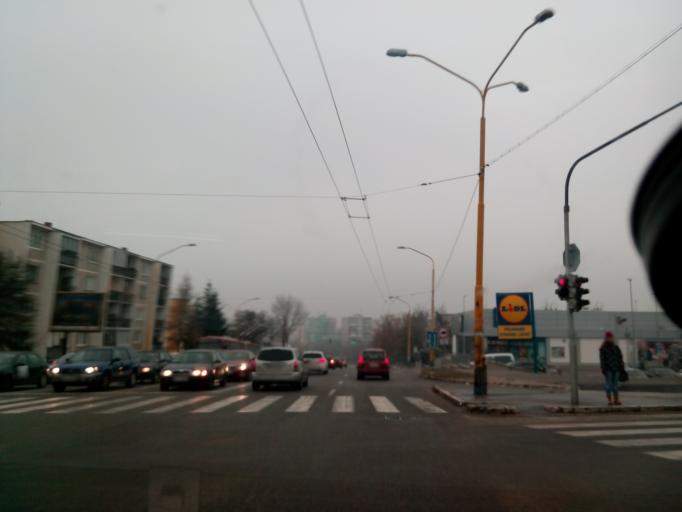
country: SK
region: Kosicky
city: Kosice
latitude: 48.7134
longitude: 21.2267
